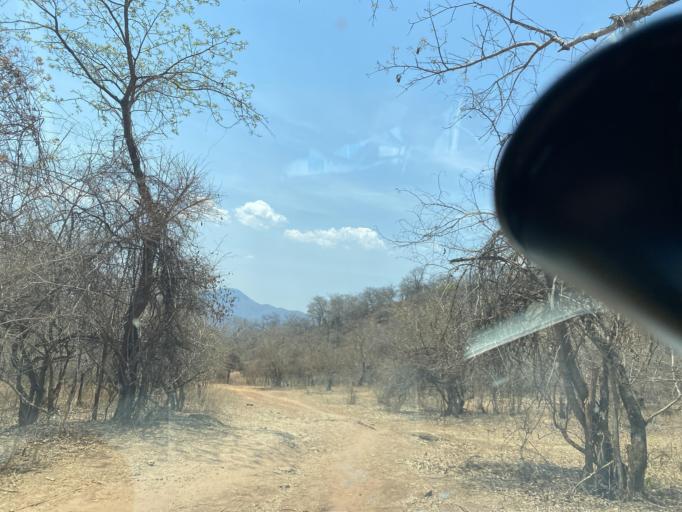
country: ZM
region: Lusaka
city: Kafue
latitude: -15.7932
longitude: 28.4562
